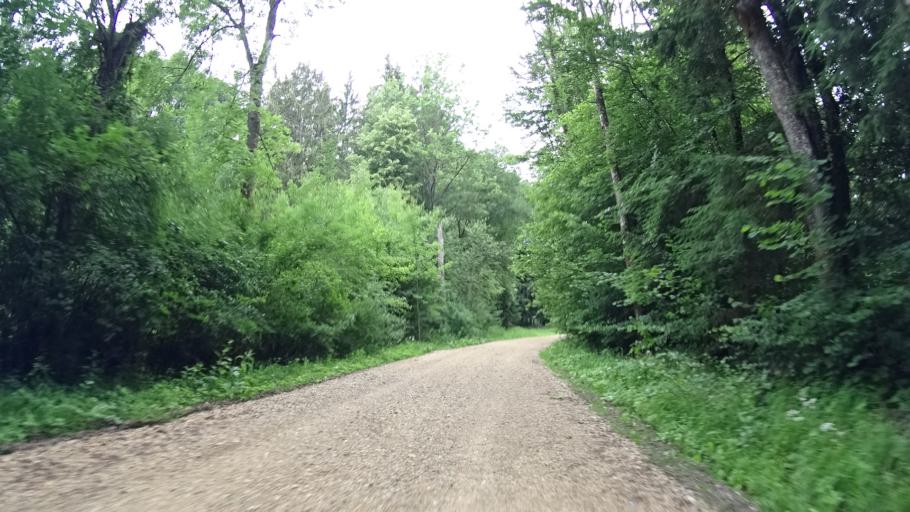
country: DE
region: Bavaria
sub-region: Upper Bavaria
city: Stammham
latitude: 48.8755
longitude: 11.5153
